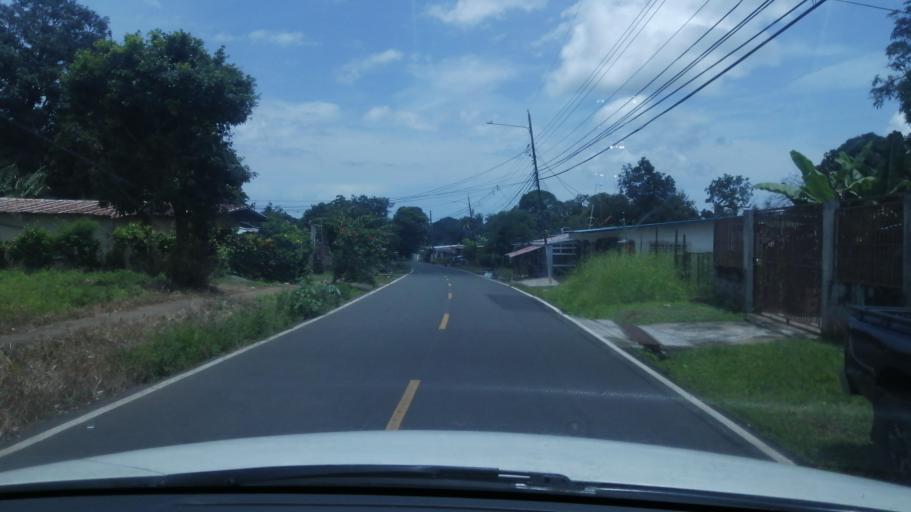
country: PA
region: Chiriqui
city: David
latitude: 8.4157
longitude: -82.4272
